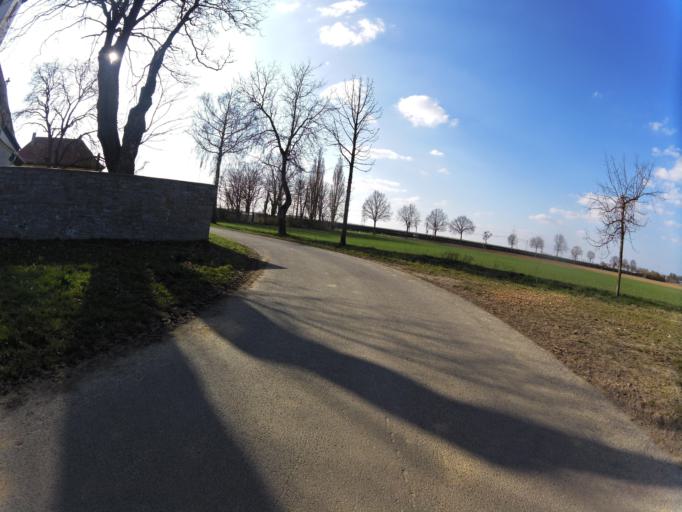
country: DE
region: Bavaria
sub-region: Regierungsbezirk Unterfranken
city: Prosselsheim
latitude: 49.8444
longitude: 10.1049
